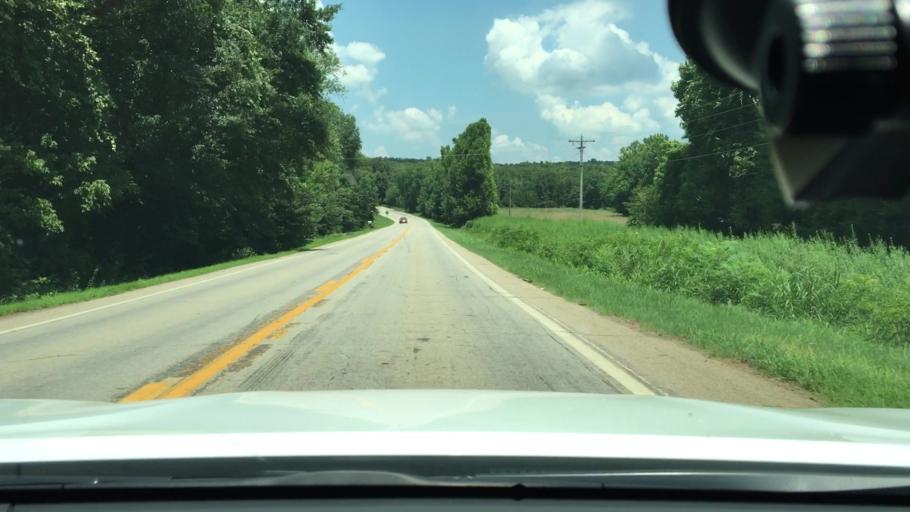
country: US
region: Arkansas
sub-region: Logan County
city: Booneville
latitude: 35.2056
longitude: -93.9244
